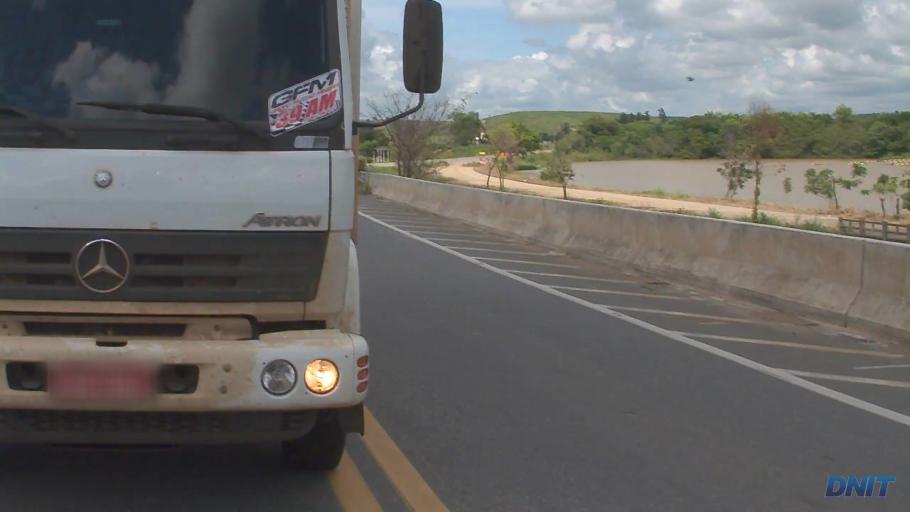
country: BR
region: Minas Gerais
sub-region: Governador Valadares
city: Governador Valadares
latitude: -19.0476
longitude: -42.1552
